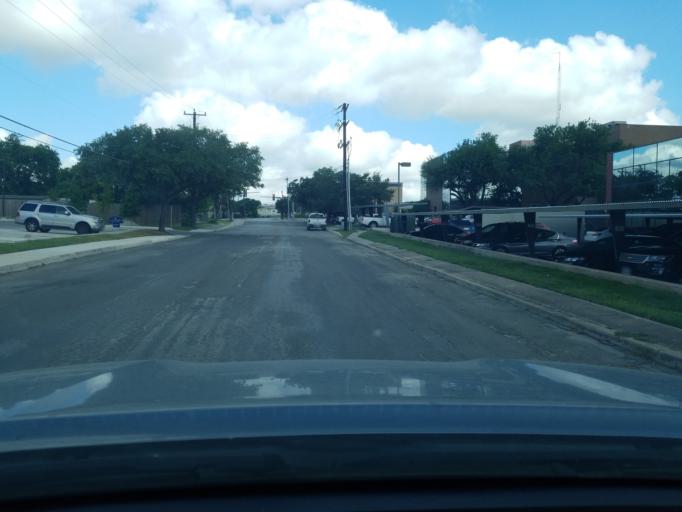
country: US
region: Texas
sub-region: Bexar County
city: Castle Hills
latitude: 29.5315
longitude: -98.4879
